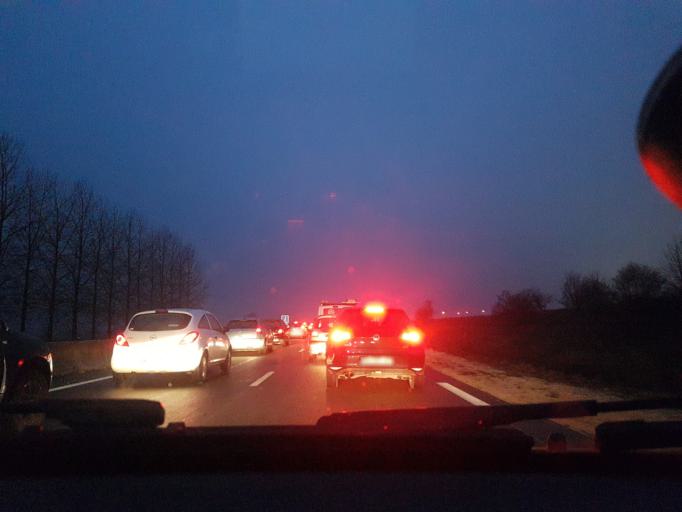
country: FR
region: Franche-Comte
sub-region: Departement du Doubs
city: Doubs
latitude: 46.9195
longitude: 6.3352
